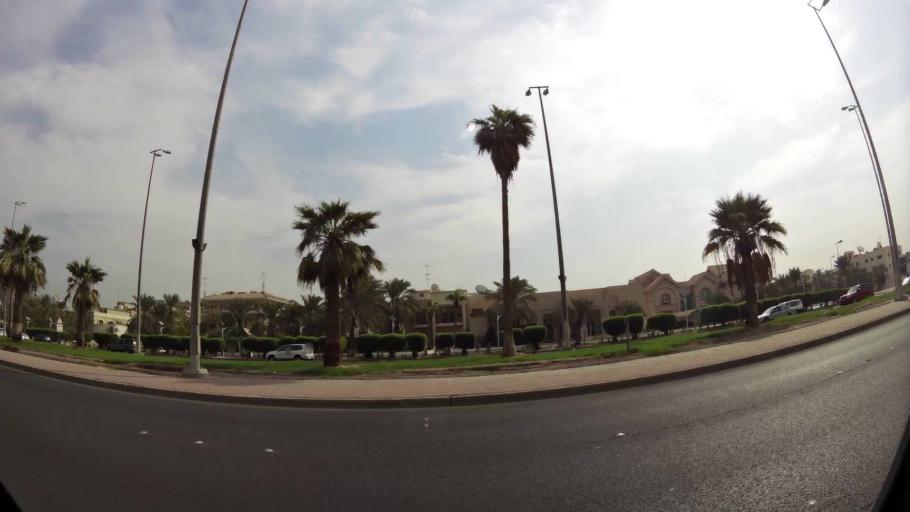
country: KW
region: Al Asimah
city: Ash Shamiyah
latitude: 29.3546
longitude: 47.9734
